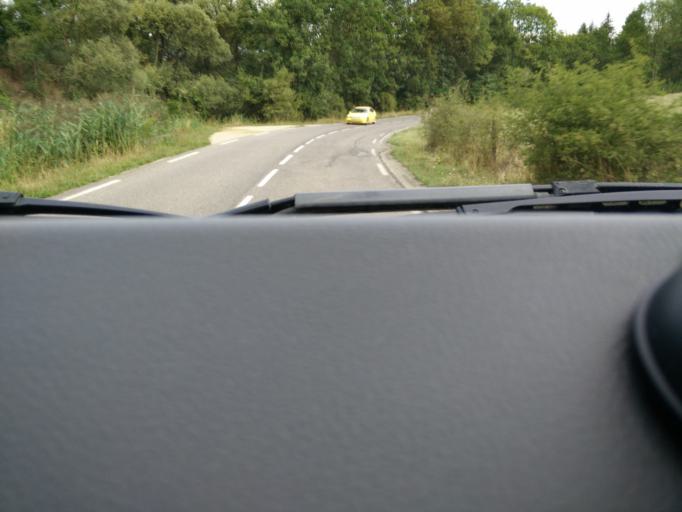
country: FR
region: Lorraine
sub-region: Departement de Meurthe-et-Moselle
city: Belleville
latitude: 48.8351
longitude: 6.0925
